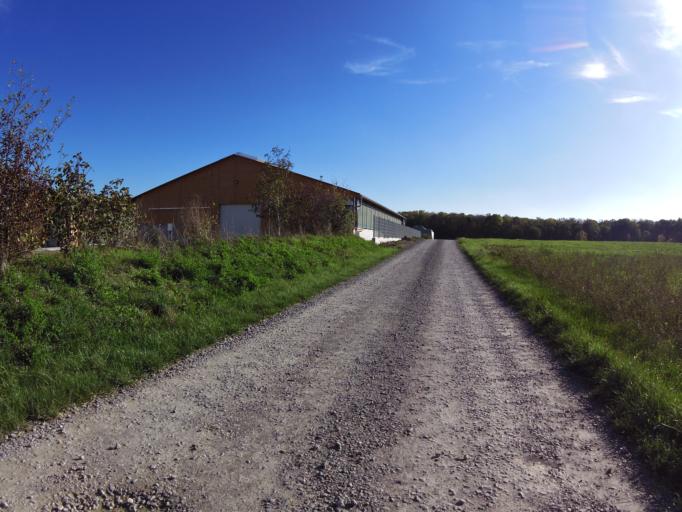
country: DE
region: Bavaria
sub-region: Regierungsbezirk Unterfranken
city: Biebelried
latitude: 49.7267
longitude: 10.0892
